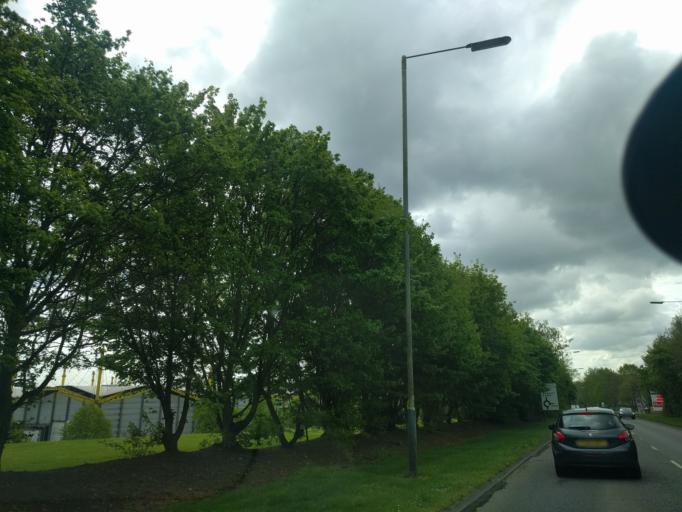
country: GB
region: England
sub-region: Wiltshire
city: Lydiard Tregoze
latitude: 51.5679
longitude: -1.8269
